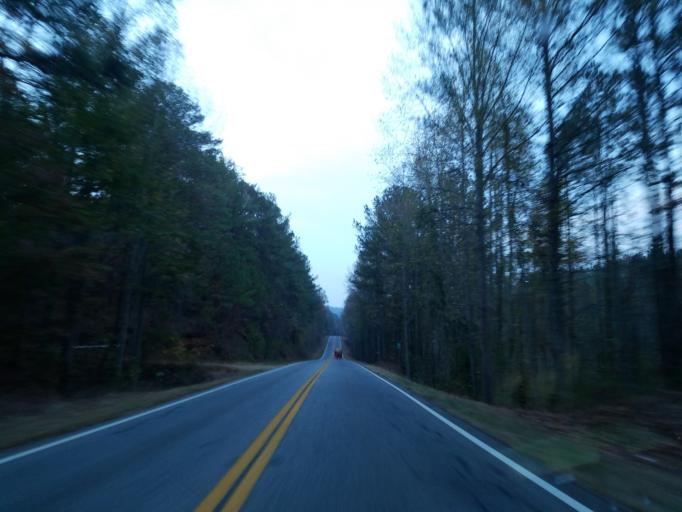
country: US
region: Georgia
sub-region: Pickens County
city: Jasper
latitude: 34.5412
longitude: -84.5811
